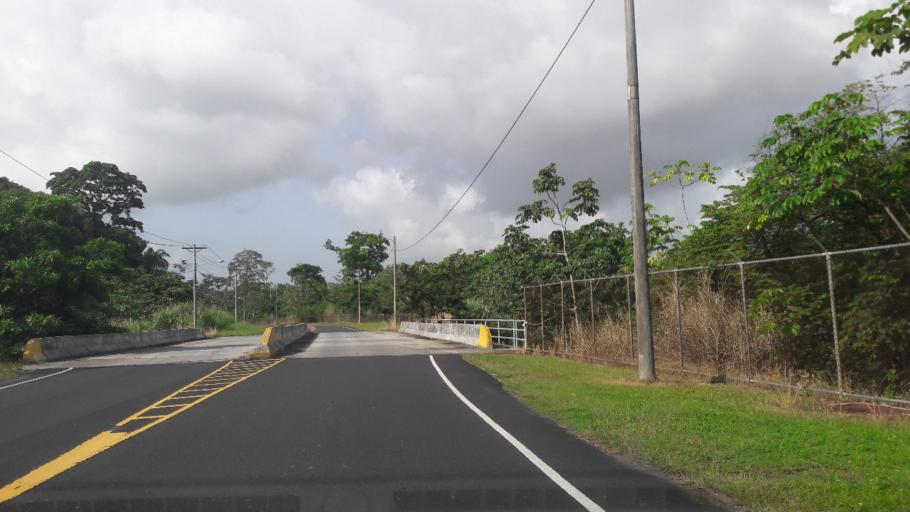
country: PA
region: Colon
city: Cativa
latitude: 9.3576
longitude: -79.8633
